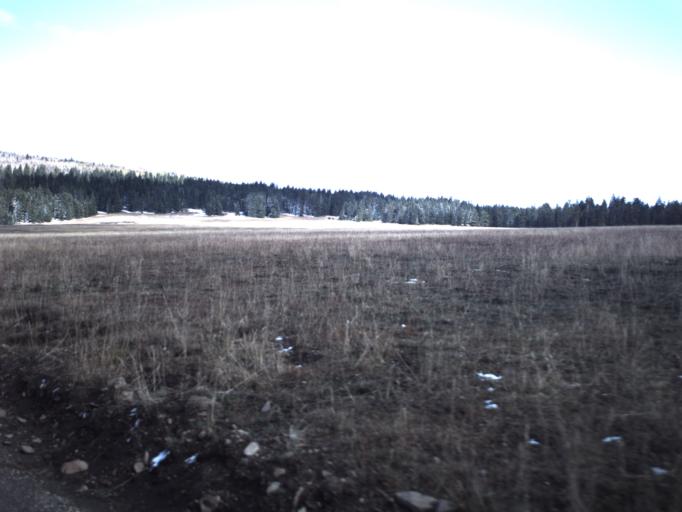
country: US
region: Utah
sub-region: Piute County
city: Junction
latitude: 38.2788
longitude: -112.3621
